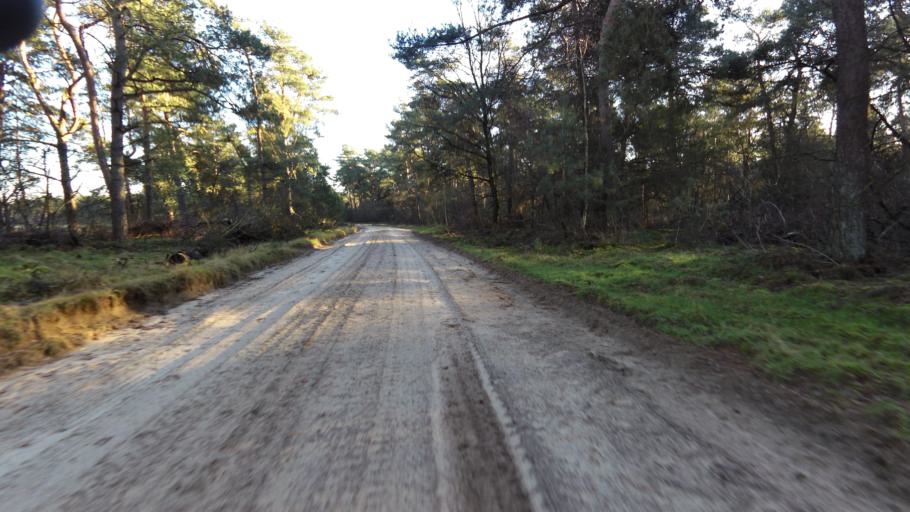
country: NL
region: Gelderland
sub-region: Gemeente Barneveld
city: Garderen
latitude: 52.2075
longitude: 5.7310
